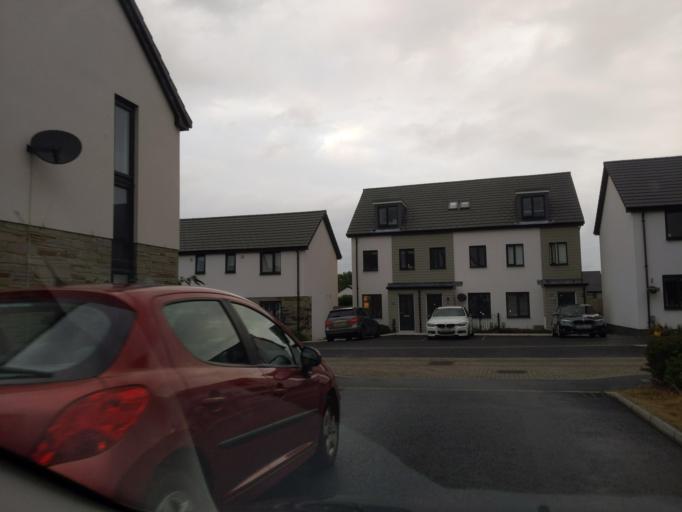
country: GB
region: England
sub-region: Plymouth
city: Plymstock
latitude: 50.3693
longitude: -4.1013
